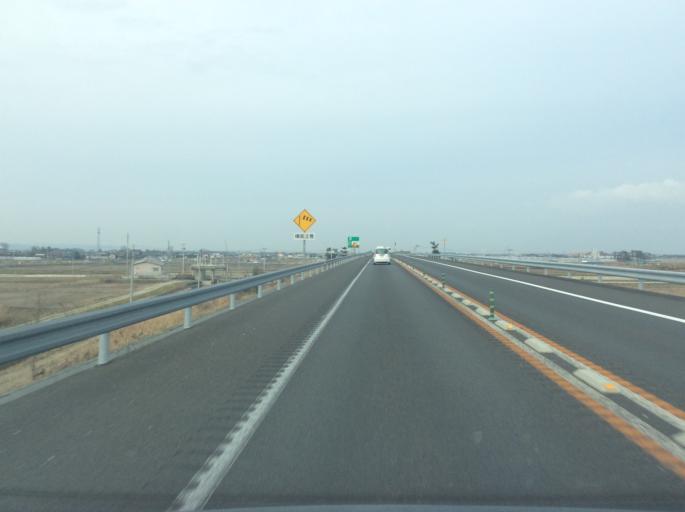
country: JP
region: Miyagi
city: Watari
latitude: 38.0316
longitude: 140.8910
